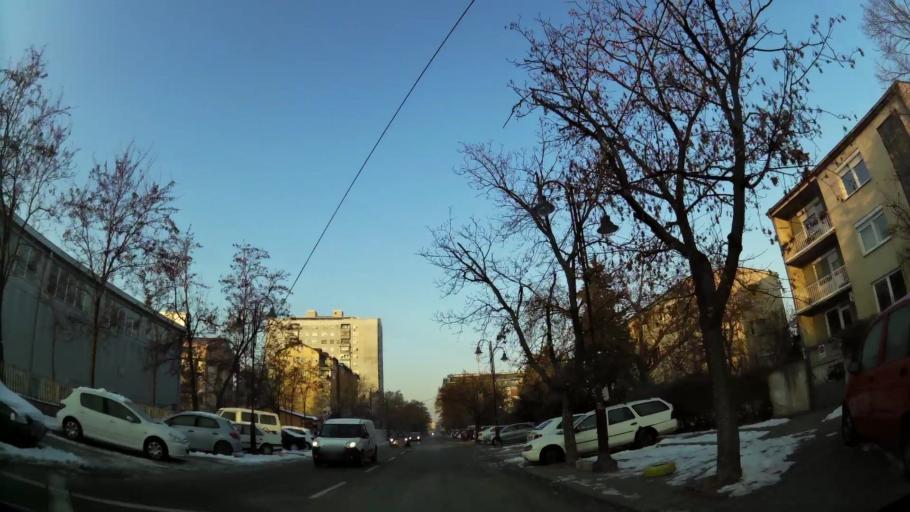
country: MK
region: Karpos
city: Skopje
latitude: 42.0049
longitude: 21.4130
